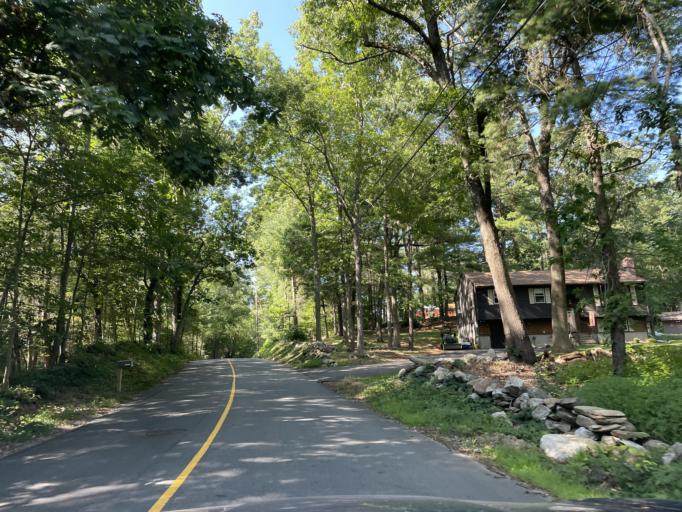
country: US
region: Massachusetts
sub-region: Worcester County
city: Charlton
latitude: 42.1368
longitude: -71.9413
